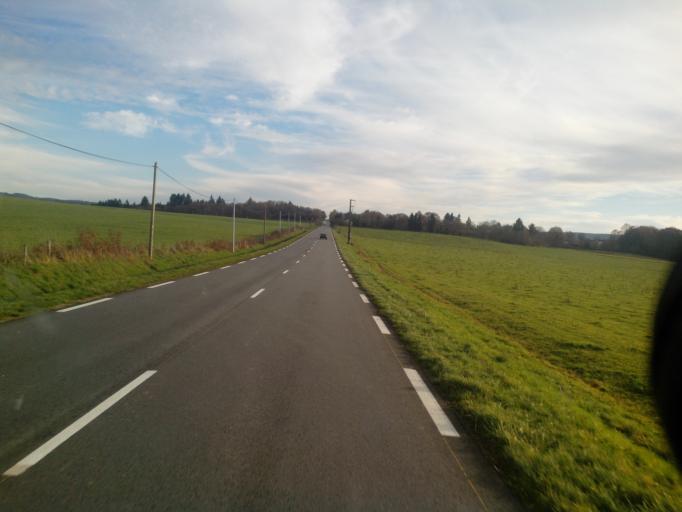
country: FR
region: Limousin
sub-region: Departement de la Haute-Vienne
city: Neuvic-Entier
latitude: 45.7495
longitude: 1.5988
